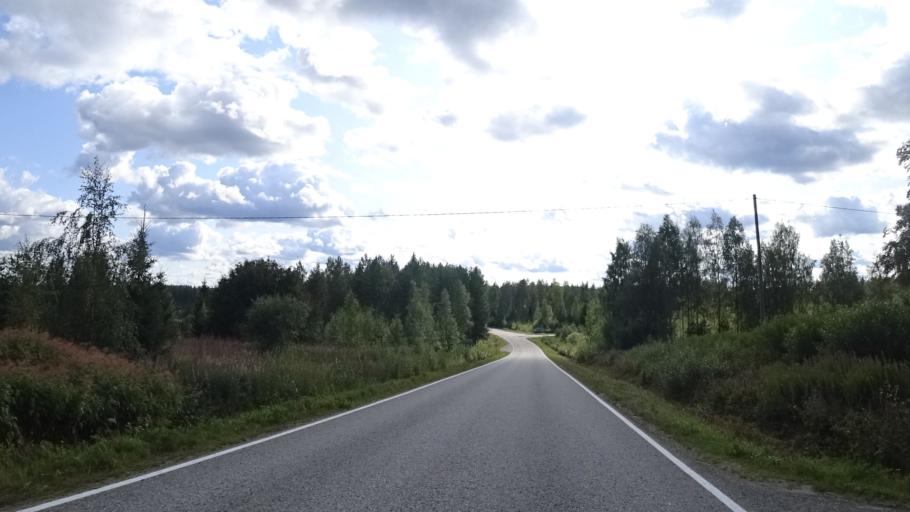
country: RU
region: Republic of Karelia
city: Vyartsilya
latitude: 62.3364
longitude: 30.8273
